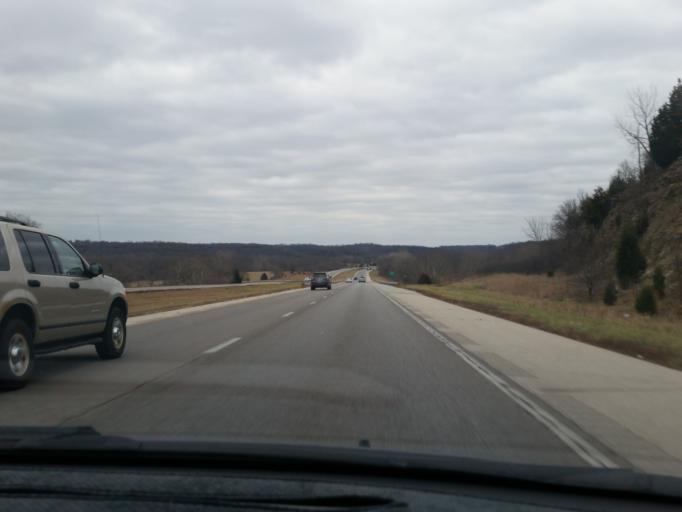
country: US
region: Kansas
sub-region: Johnson County
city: De Soto
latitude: 38.9585
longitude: -94.9255
